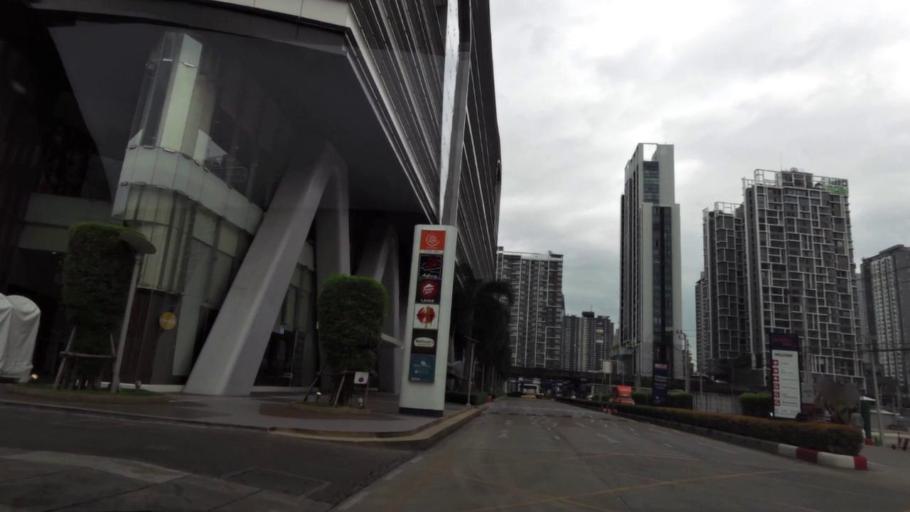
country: TH
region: Bangkok
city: Din Daeng
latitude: 13.7575
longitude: 100.5673
